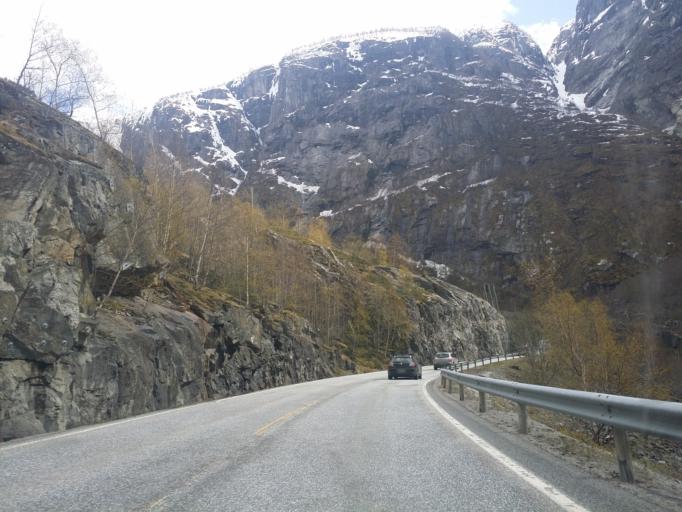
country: NO
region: Hordaland
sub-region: Eidfjord
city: Eidfjord
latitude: 60.4191
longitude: 7.1919
